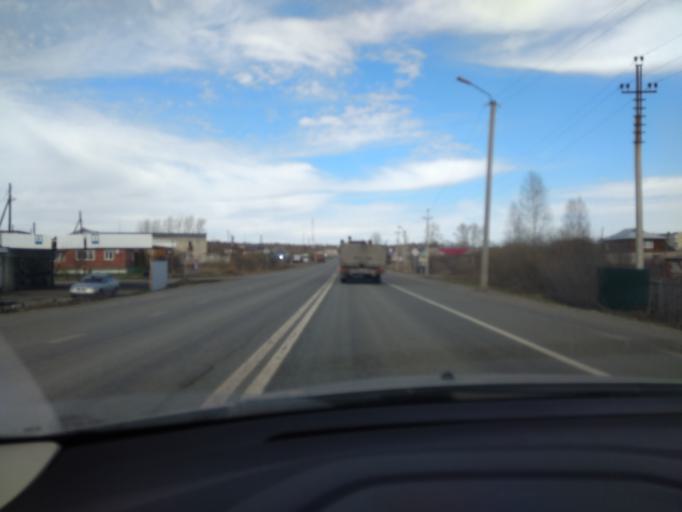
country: RU
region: Sverdlovsk
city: Pyshma
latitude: 56.9476
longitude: 63.2234
